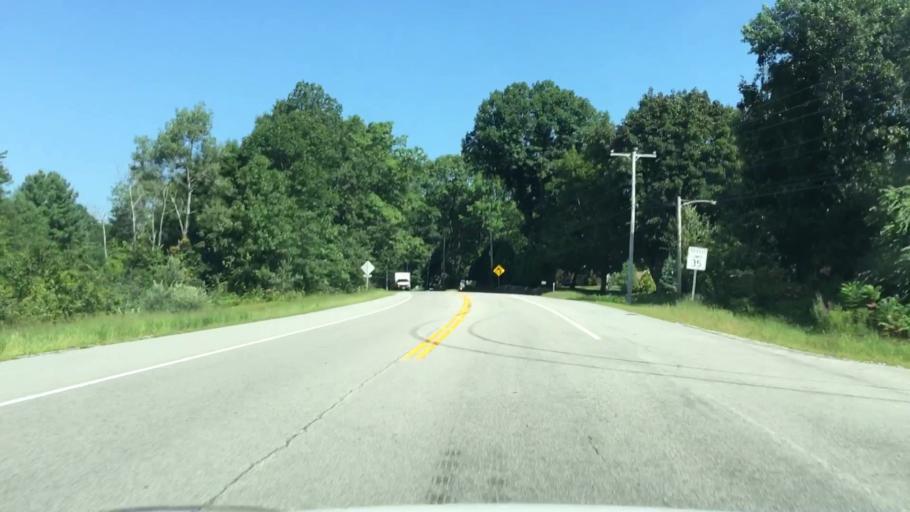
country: US
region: New Hampshire
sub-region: Rockingham County
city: Seabrook
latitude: 42.9041
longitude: -70.9105
